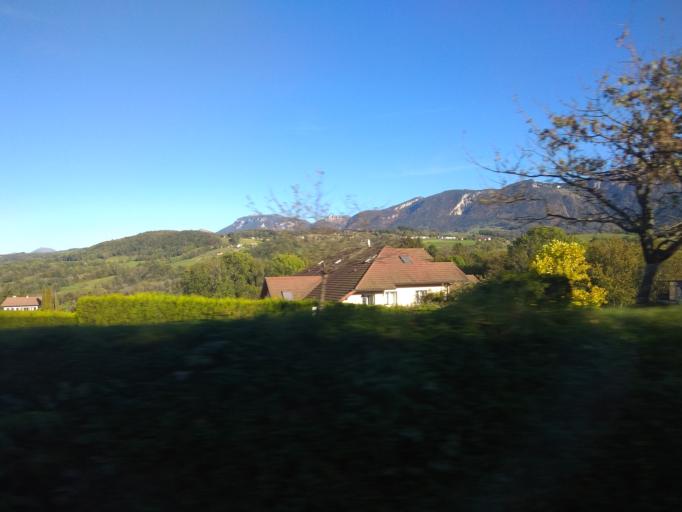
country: FR
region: Rhone-Alpes
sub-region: Departement de la Haute-Savoie
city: Saint-Martin-Bellevue
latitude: 45.9795
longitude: 6.1567
